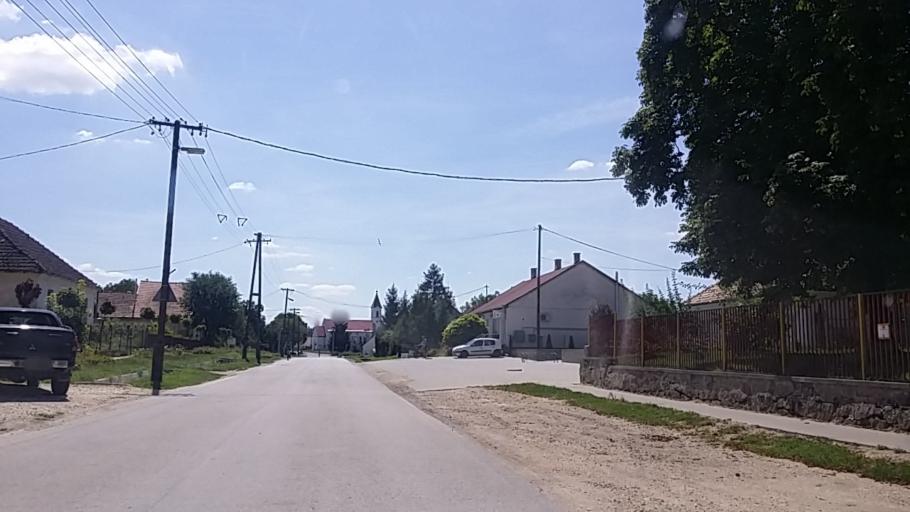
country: HU
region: Fejer
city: Deg
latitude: 46.8717
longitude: 18.4432
